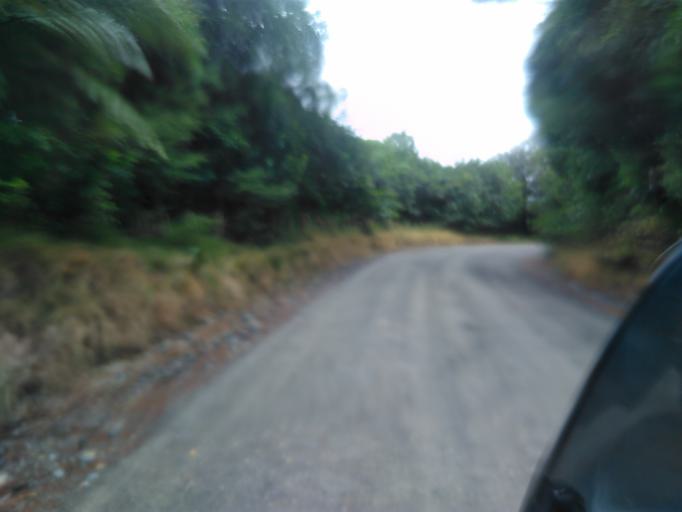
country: NZ
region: Gisborne
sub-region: Gisborne District
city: Gisborne
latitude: -38.2375
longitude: 178.0700
